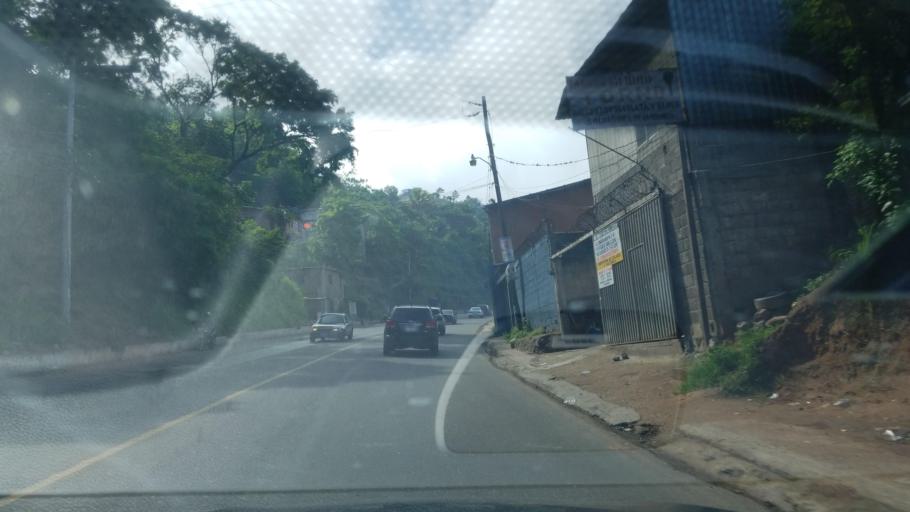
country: HN
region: Francisco Morazan
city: El Tablon
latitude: 14.0577
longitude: -87.1601
